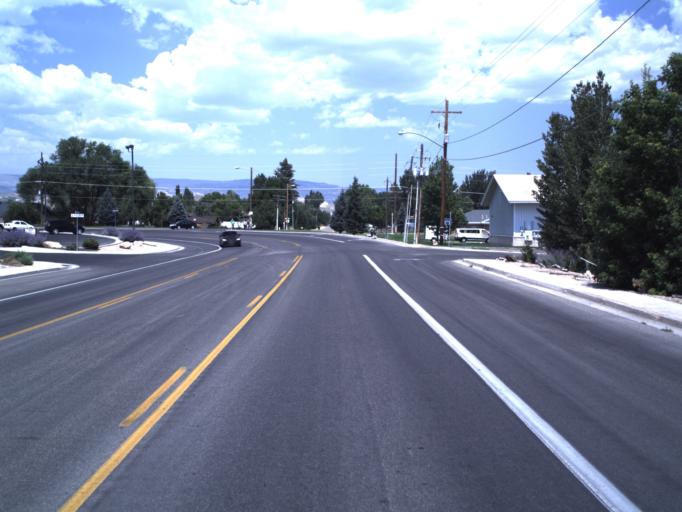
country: US
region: Utah
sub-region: Uintah County
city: Vernal
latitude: 40.4614
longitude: -109.5382
